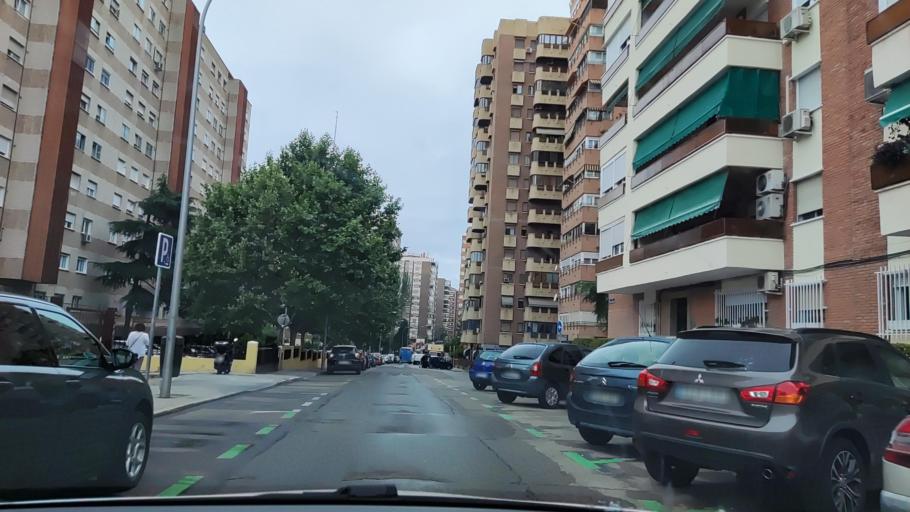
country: ES
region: Madrid
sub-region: Provincia de Madrid
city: Tetuan de las Victorias
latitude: 40.4861
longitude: -3.7015
